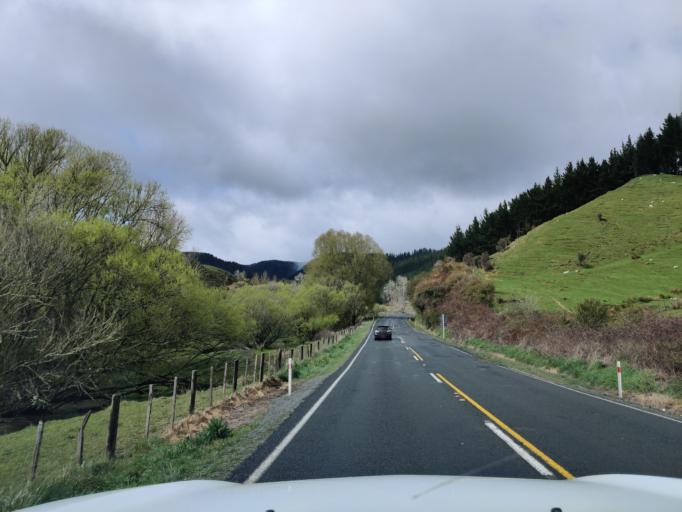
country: NZ
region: Waikato
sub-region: Otorohanga District
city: Otorohanga
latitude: -38.6115
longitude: 175.2182
